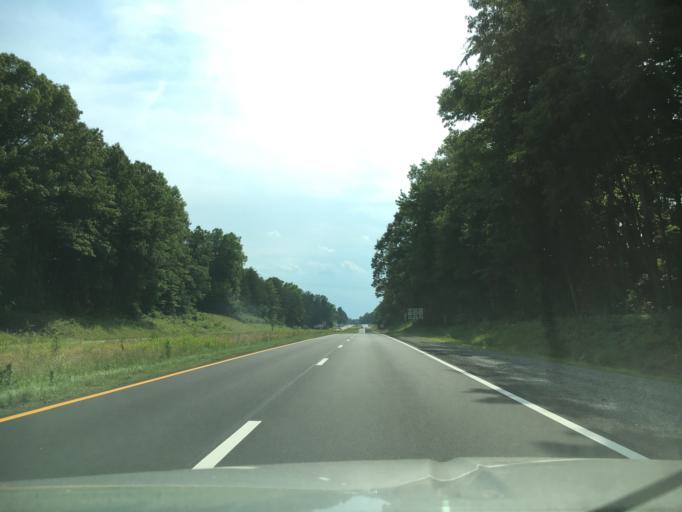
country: US
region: Virginia
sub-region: Halifax County
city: Halifax
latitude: 36.8186
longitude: -78.7312
